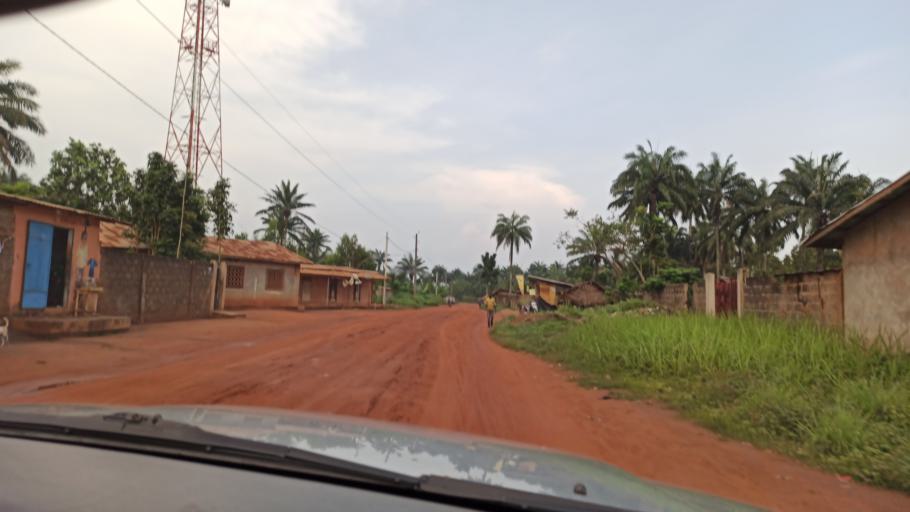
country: BJ
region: Queme
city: Porto-Novo
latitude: 6.4966
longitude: 2.6956
